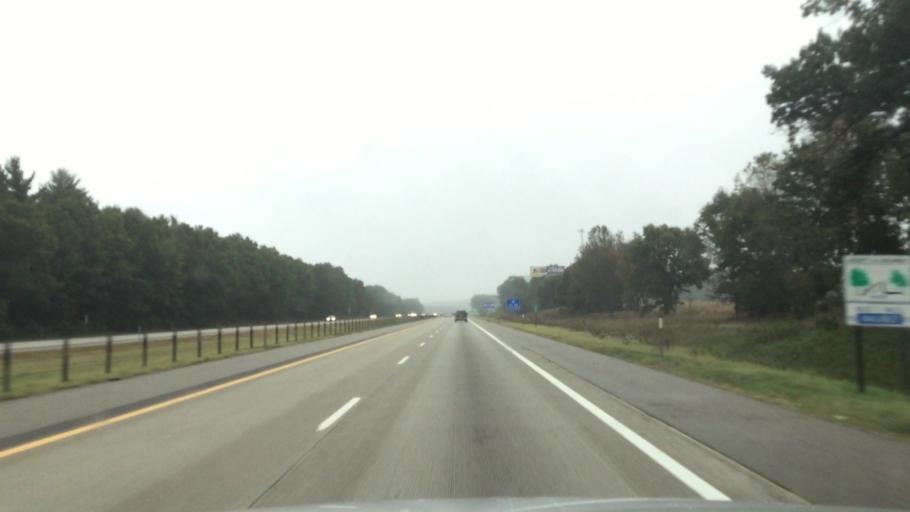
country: US
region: Michigan
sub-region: Van Buren County
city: Mattawan
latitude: 42.2215
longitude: -85.8027
